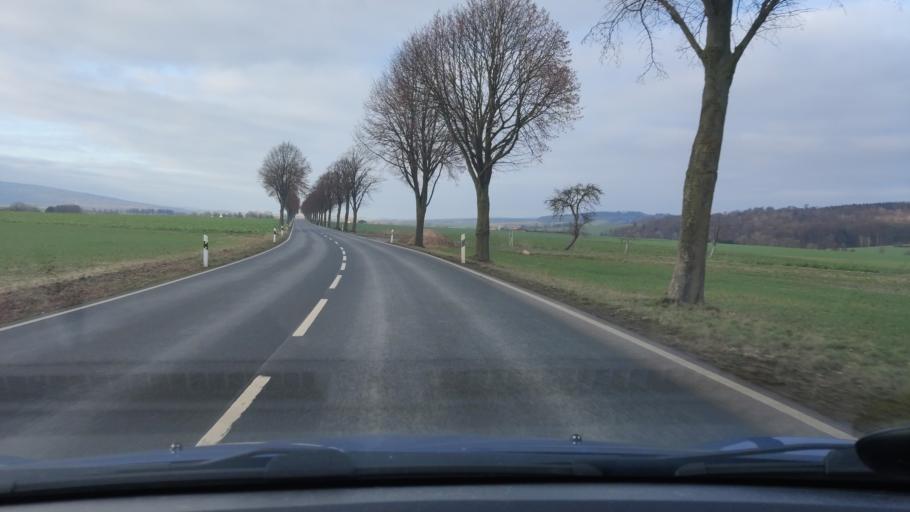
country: DE
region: Lower Saxony
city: Coppenbrugge
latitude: 52.1427
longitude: 9.5137
